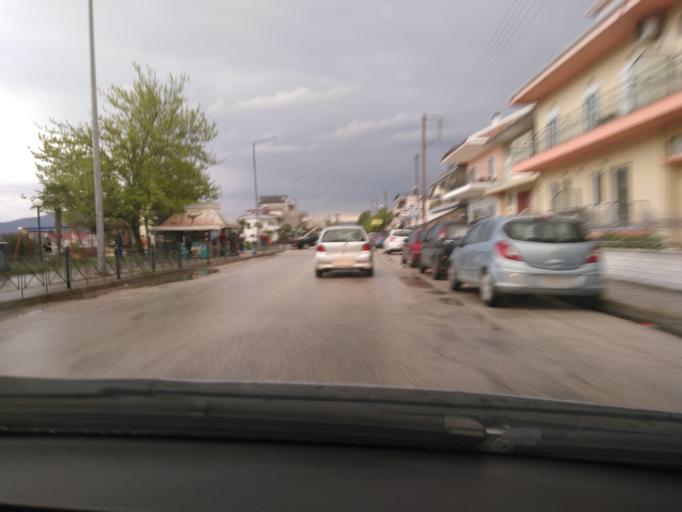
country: GR
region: Epirus
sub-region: Nomos Ioanninon
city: Anatoli
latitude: 39.6403
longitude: 20.8677
